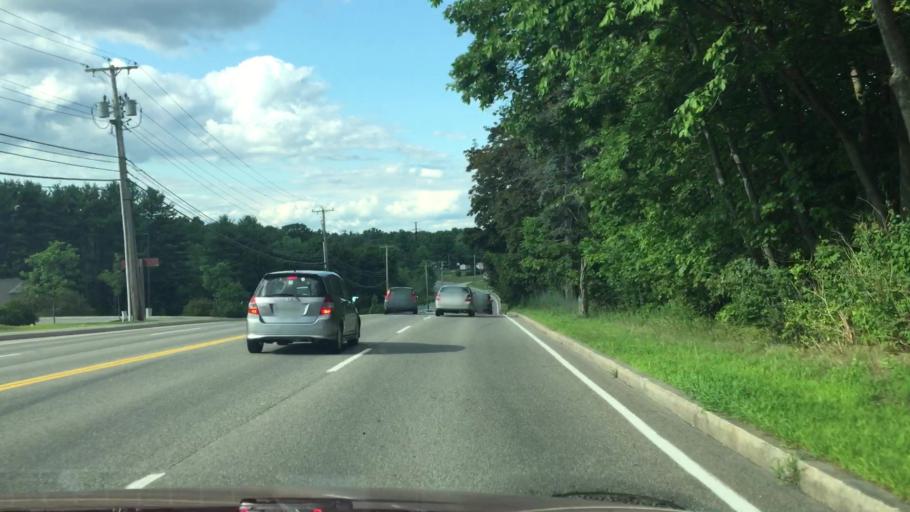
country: US
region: Maine
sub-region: York County
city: Saco
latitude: 43.5158
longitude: -70.4291
